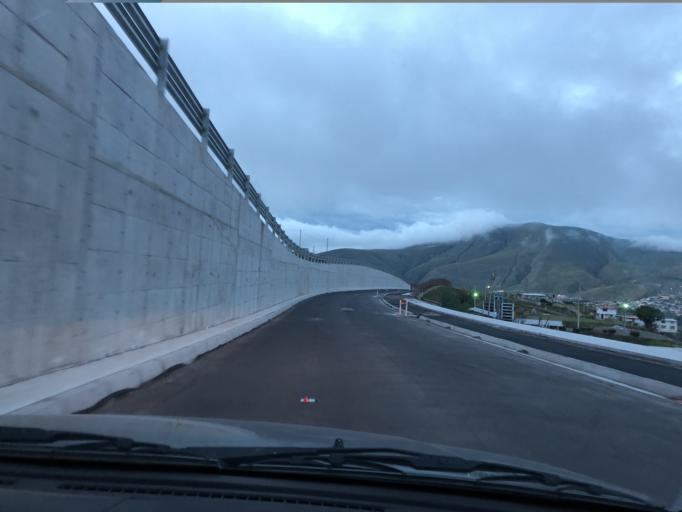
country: EC
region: Imbabura
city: Ibarra
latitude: 0.3728
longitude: -78.1284
